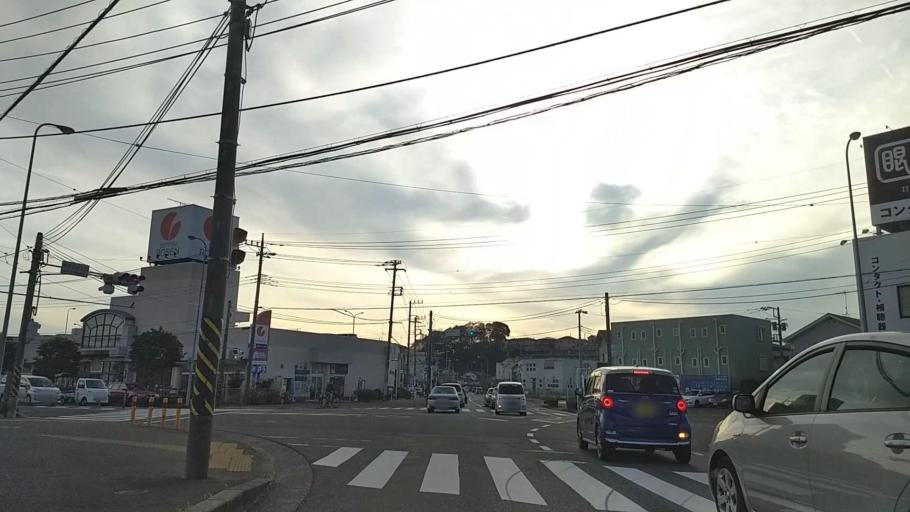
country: JP
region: Kanagawa
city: Atsugi
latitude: 35.4564
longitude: 139.3517
